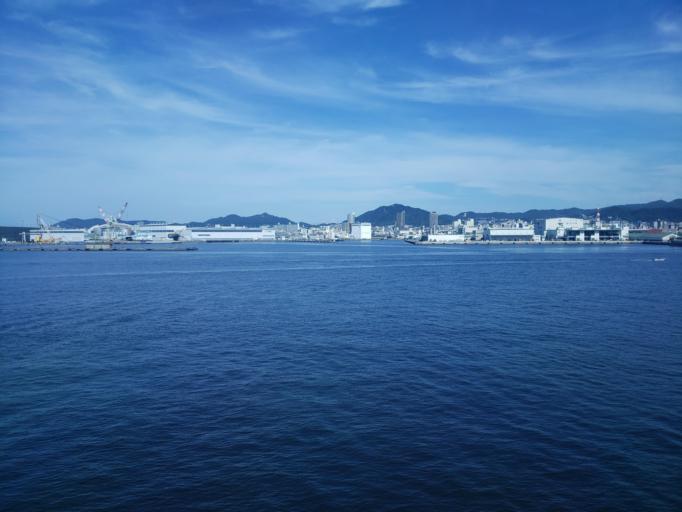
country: JP
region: Hyogo
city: Kobe
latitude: 34.6595
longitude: 135.1895
